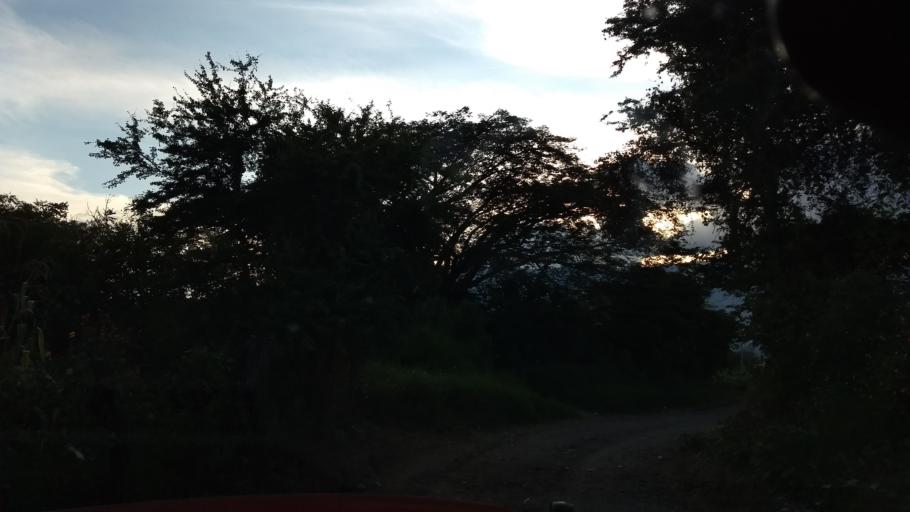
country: MX
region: Jalisco
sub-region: San Gabriel
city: Alista
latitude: 19.5017
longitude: -103.7636
